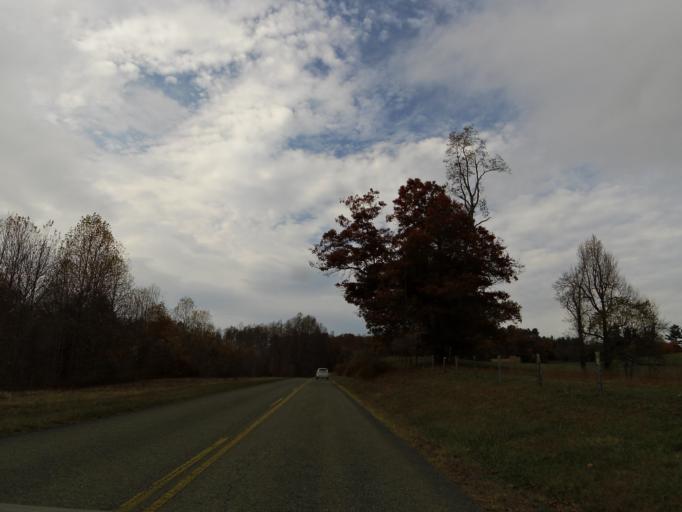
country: US
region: Virginia
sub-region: Carroll County
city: Woodlawn
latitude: 36.6088
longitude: -80.8203
